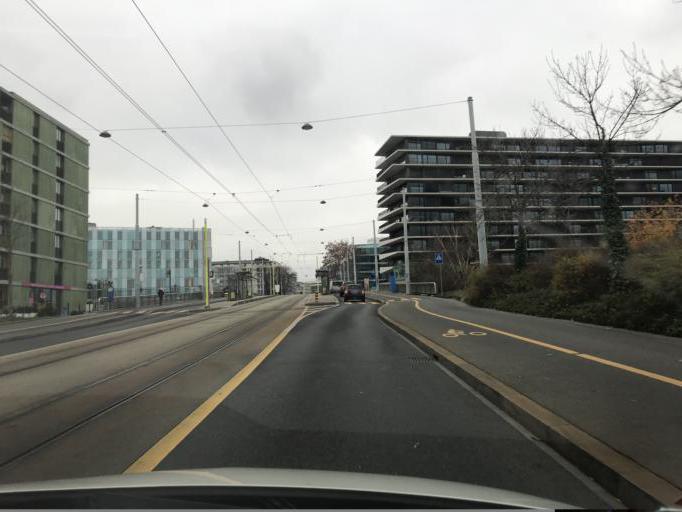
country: CH
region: Geneva
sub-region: Geneva
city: Geneve
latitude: 46.2198
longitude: 6.1465
